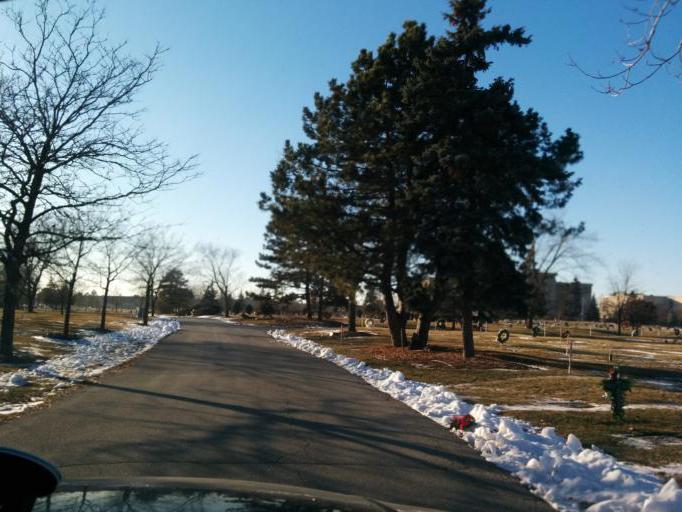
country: CA
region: Ontario
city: Etobicoke
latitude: 43.7488
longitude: -79.6110
